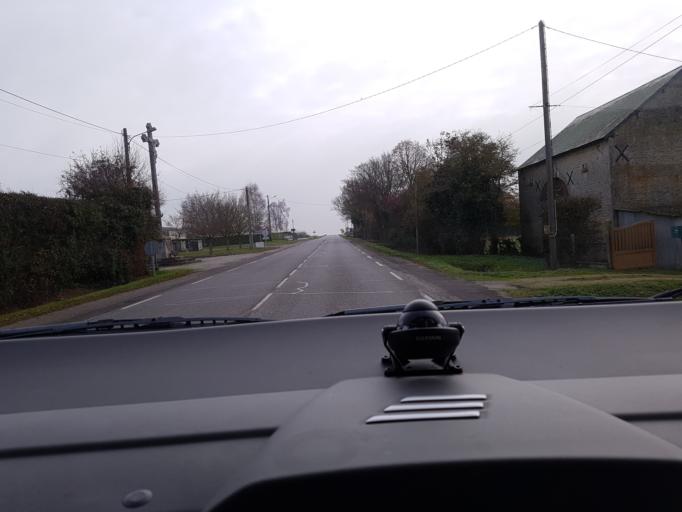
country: FR
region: Lower Normandy
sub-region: Departement de l'Orne
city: Mortree
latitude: 48.6390
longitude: 0.0806
